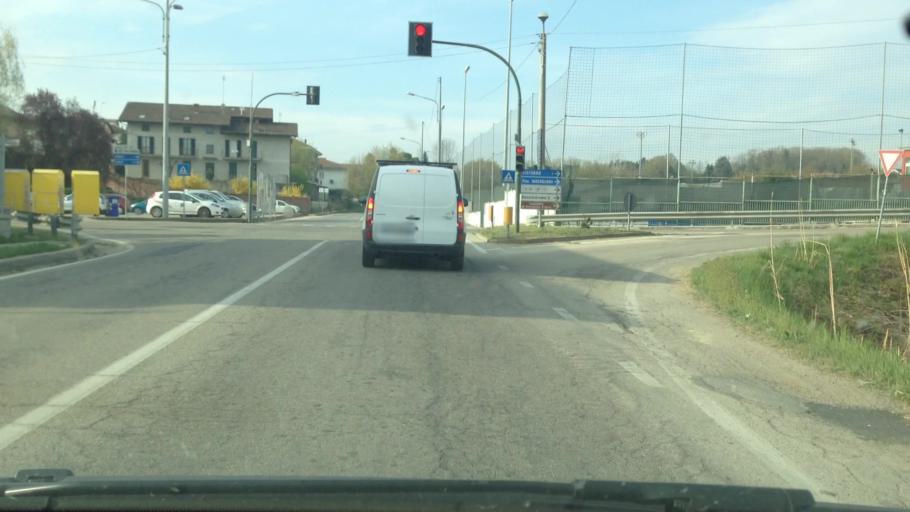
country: IT
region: Piedmont
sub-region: Provincia di Asti
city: San Damiano d'Asti
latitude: 44.8349
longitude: 8.0624
